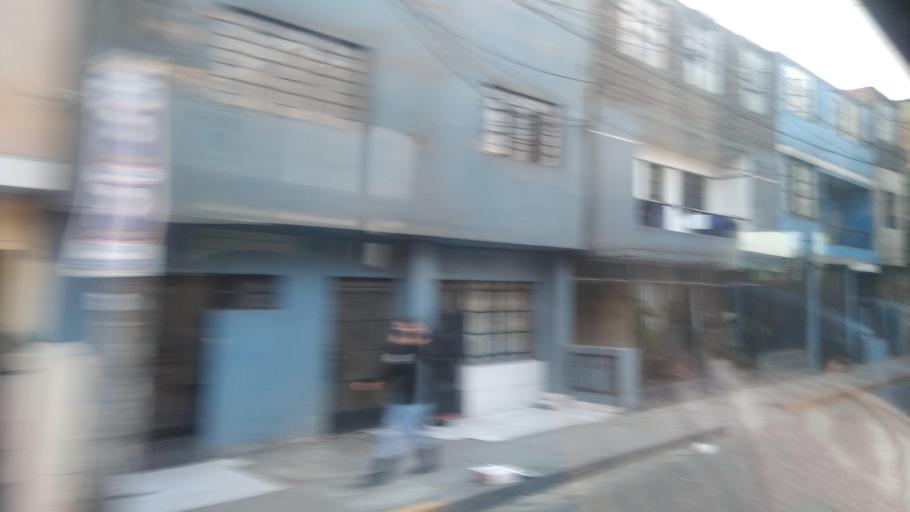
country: PE
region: Lima
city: Lima
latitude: -12.0221
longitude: -77.0007
